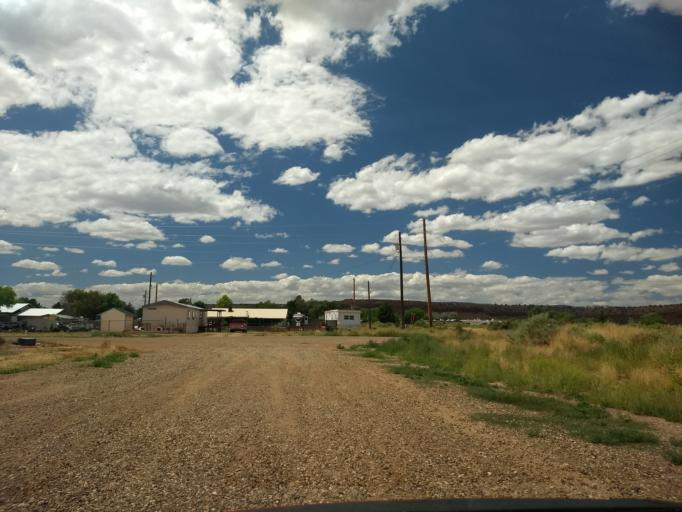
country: US
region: Arizona
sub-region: Coconino County
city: Fredonia
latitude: 36.9568
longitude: -112.5239
